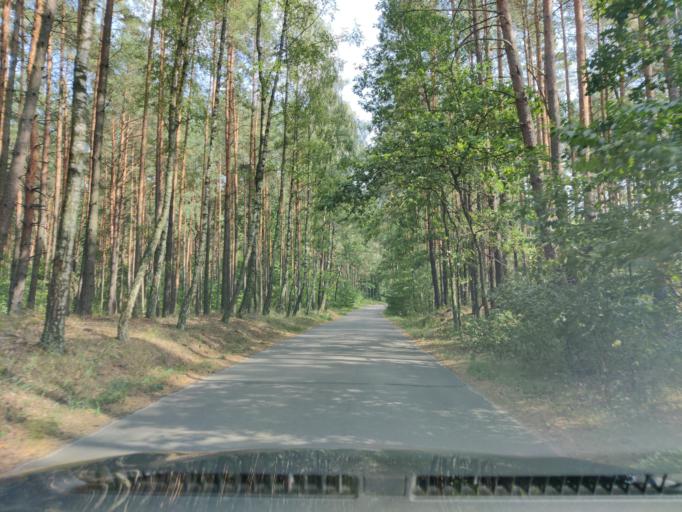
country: PL
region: Masovian Voivodeship
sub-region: Powiat makowski
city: Rozan
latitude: 52.8670
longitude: 21.4424
